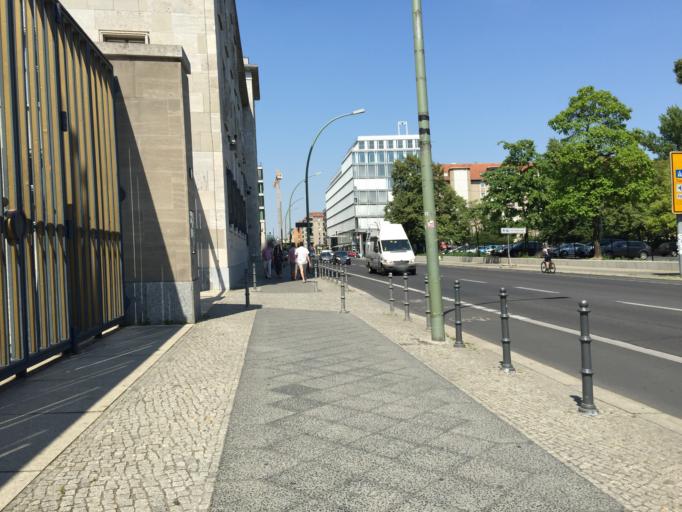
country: DE
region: Berlin
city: Tiergarten Bezirk
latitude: 52.5088
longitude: 13.3847
